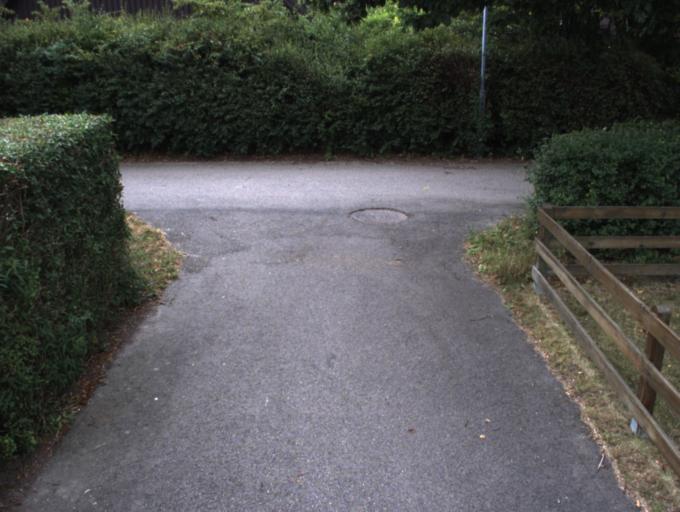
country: SE
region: Skane
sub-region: Helsingborg
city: Barslov
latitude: 56.0065
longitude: 12.8009
